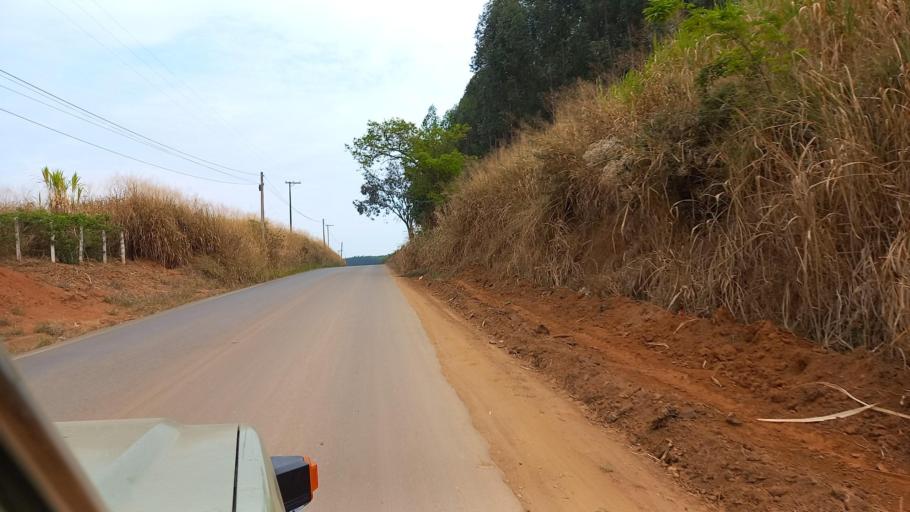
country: BR
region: Sao Paulo
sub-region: Moji-Guacu
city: Mogi-Gaucu
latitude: -22.3298
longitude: -46.8590
